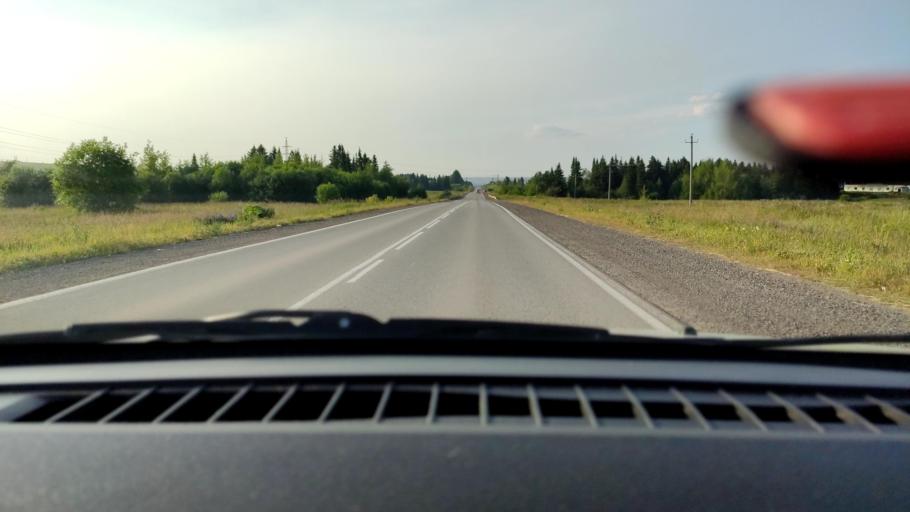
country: RU
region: Perm
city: Lobanovo
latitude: 57.8510
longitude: 56.2963
